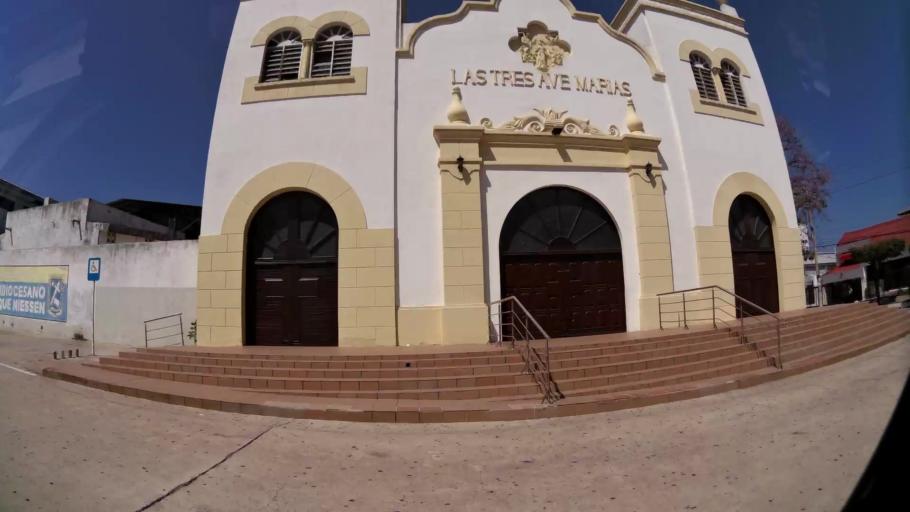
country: CO
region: Atlantico
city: Barranquilla
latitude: 11.0154
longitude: -74.8079
